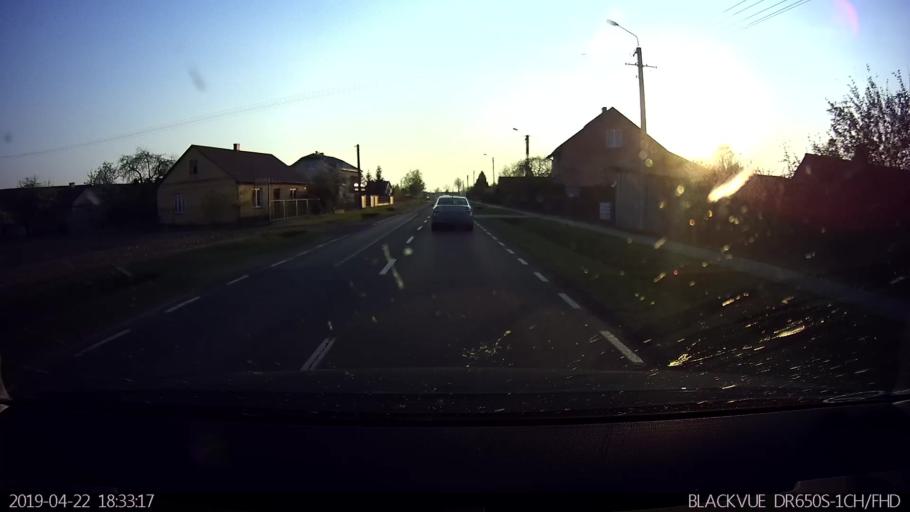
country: PL
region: Masovian Voivodeship
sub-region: Powiat wolominski
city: Jasienica
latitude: 52.4489
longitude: 21.3892
